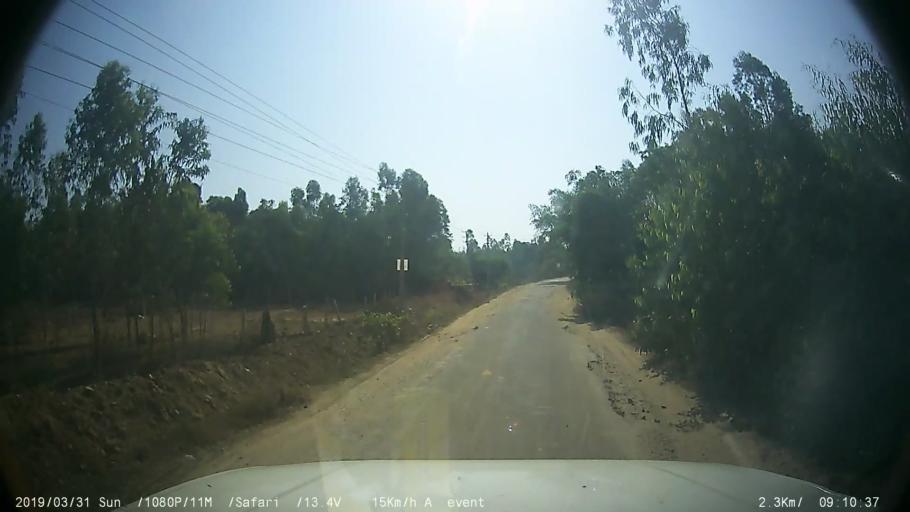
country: IN
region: Karnataka
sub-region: Bangalore Urban
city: Anekal
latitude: 12.8142
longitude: 77.6331
